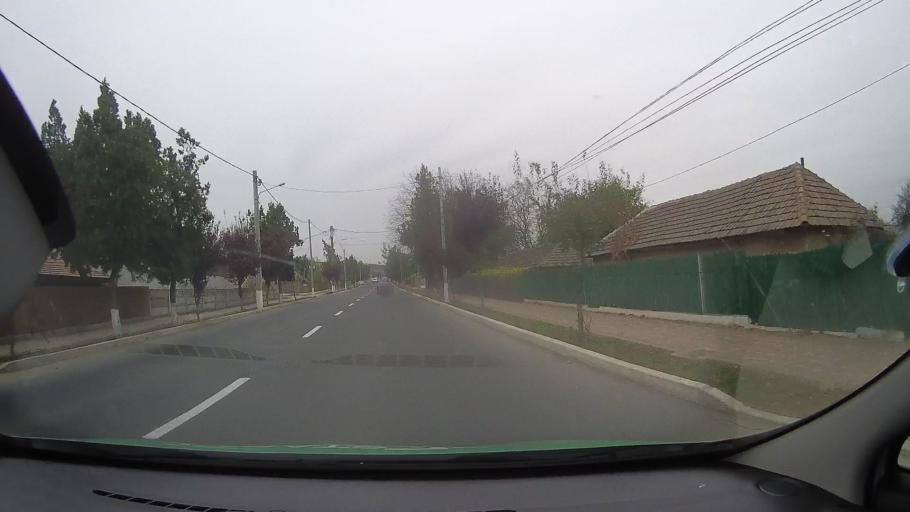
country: RO
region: Constanta
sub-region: Oras Harsova
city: Harsova
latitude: 44.6886
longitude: 27.9483
